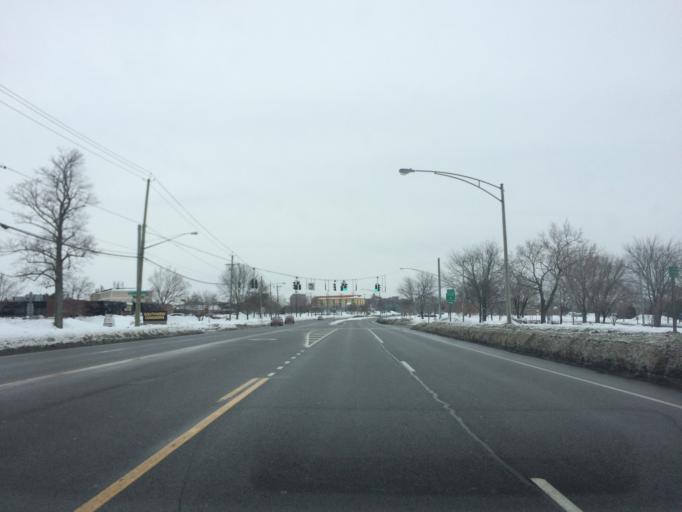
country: US
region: New York
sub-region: Monroe County
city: Rochester
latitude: 43.1020
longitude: -77.6148
